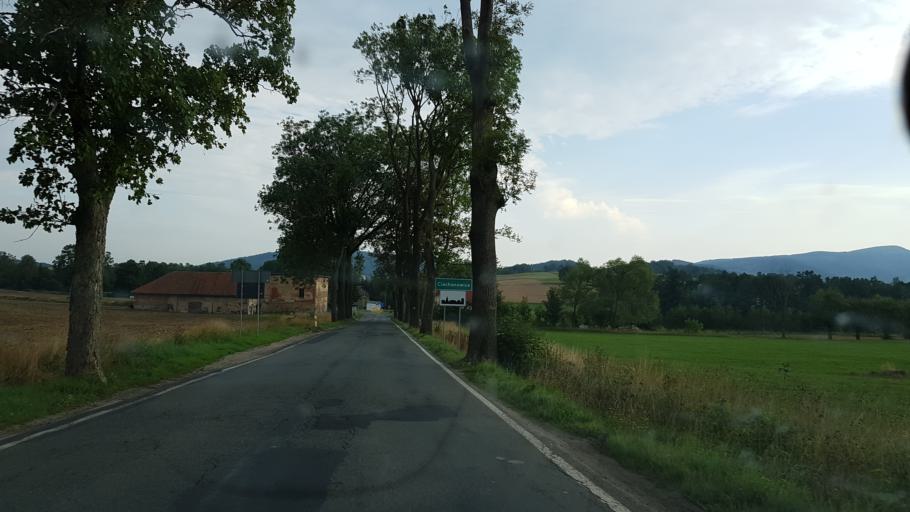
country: PL
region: Lower Silesian Voivodeship
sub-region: Powiat kamiennogorski
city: Marciszow
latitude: 50.8684
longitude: 15.9983
